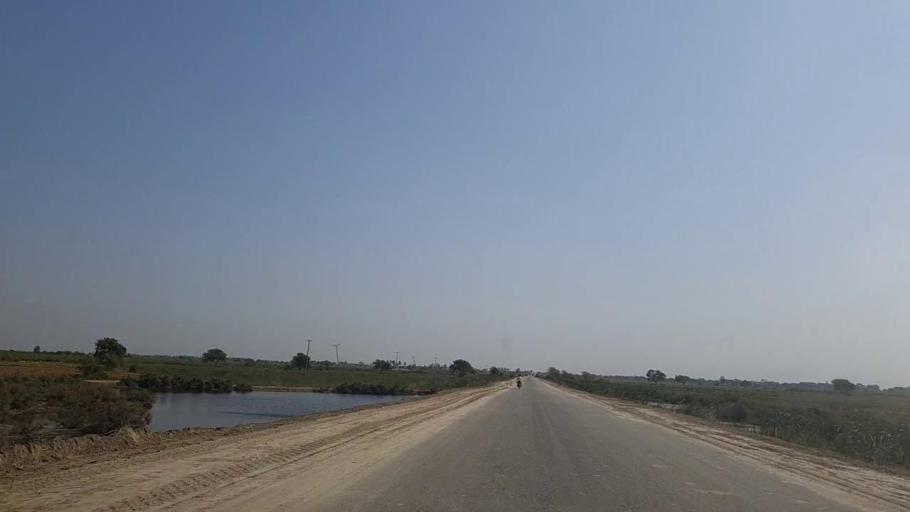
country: PK
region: Sindh
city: Daro Mehar
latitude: 24.7885
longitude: 68.1894
